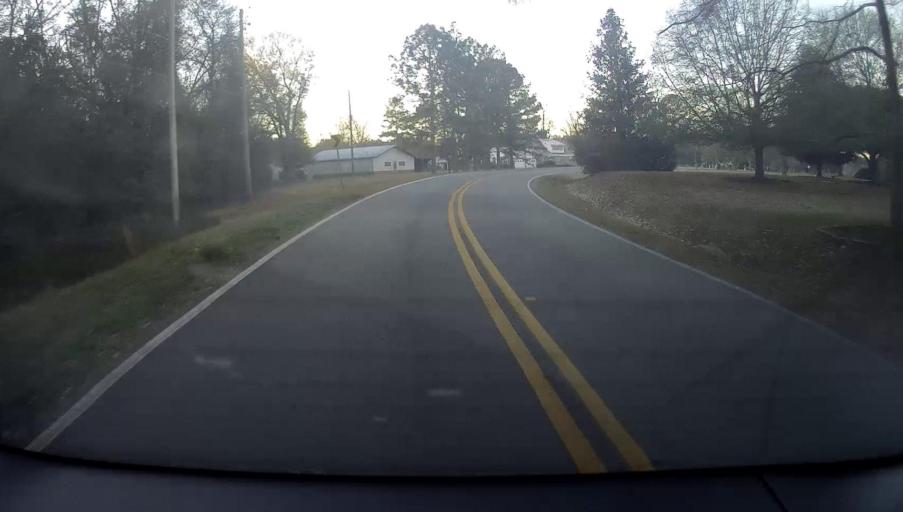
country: US
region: Georgia
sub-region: Houston County
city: Centerville
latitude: 32.6439
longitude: -83.6991
